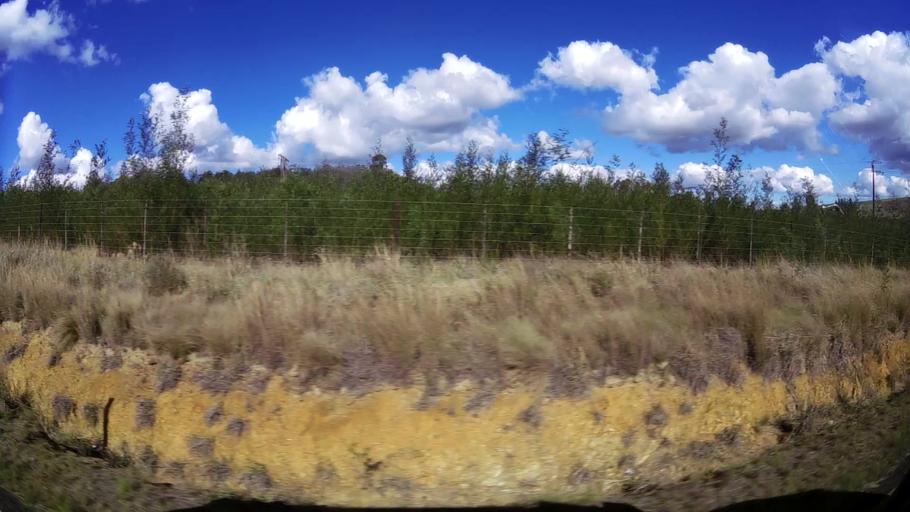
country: ZA
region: Western Cape
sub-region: Overberg District Municipality
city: Swellendam
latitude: -34.0254
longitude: 20.4231
